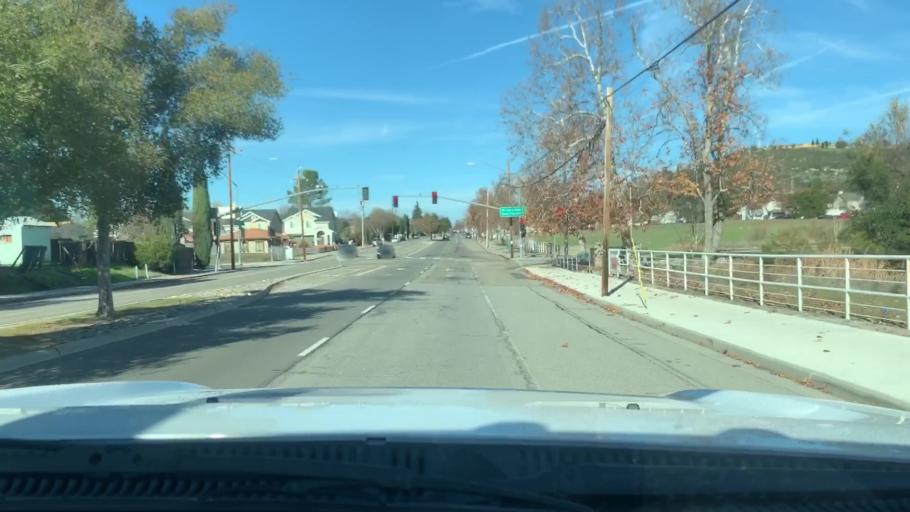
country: US
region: California
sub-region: San Luis Obispo County
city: Atascadero
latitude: 35.4596
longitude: -120.6431
